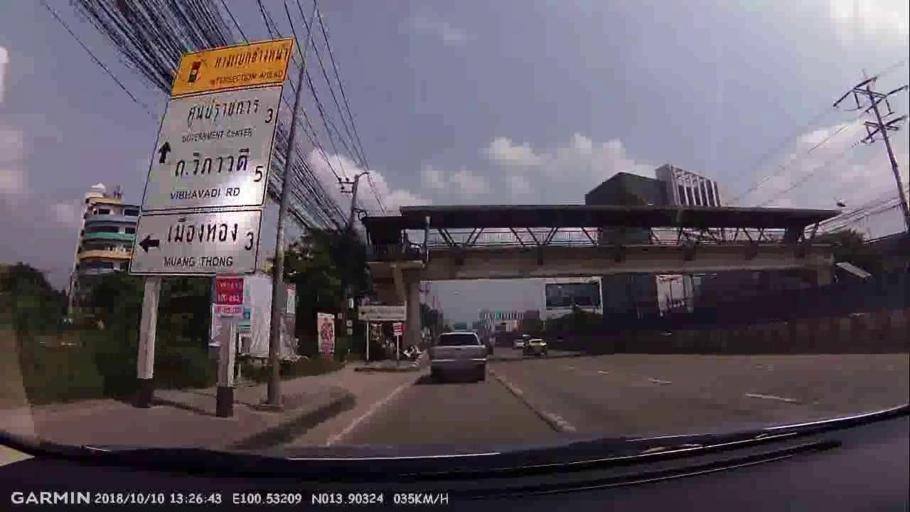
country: TH
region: Nonthaburi
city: Pak Kret
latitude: 13.9032
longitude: 100.5321
